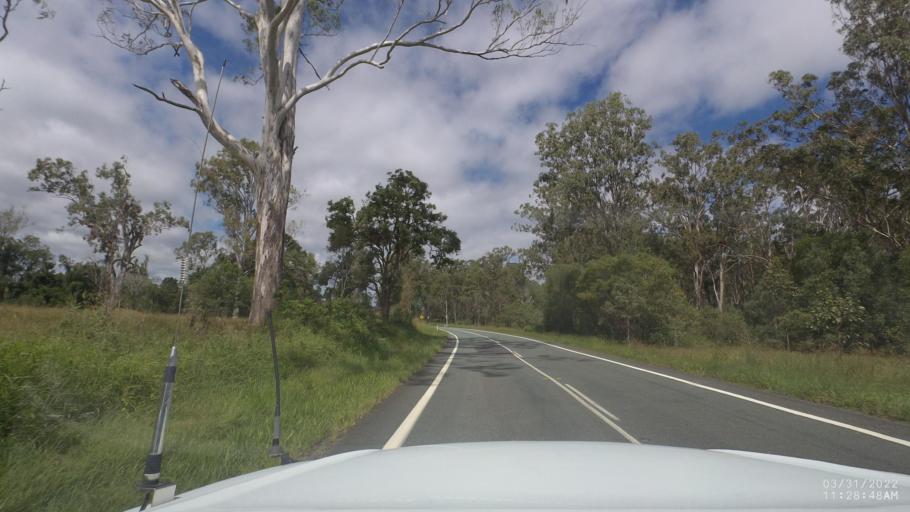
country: AU
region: Queensland
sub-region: Logan
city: Cedar Vale
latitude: -27.9299
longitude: 153.0797
